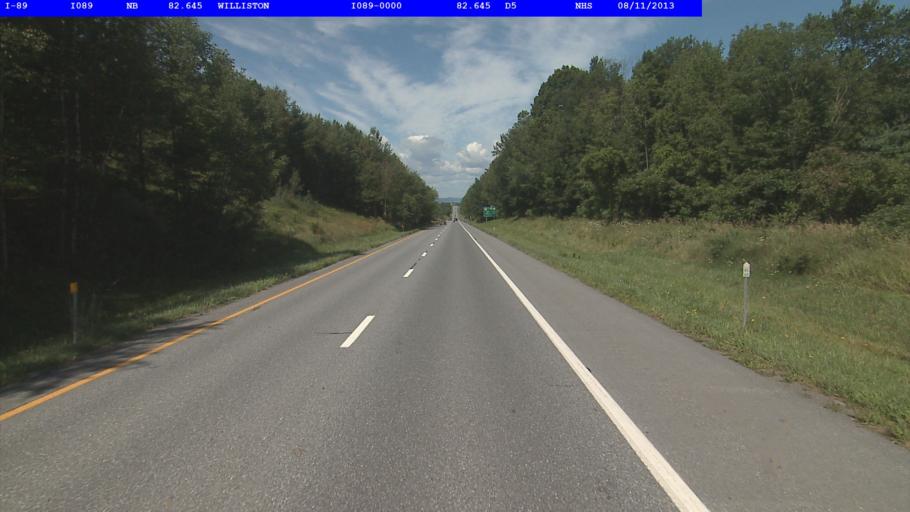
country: US
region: Vermont
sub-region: Chittenden County
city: Williston
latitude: 44.4370
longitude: -73.0887
